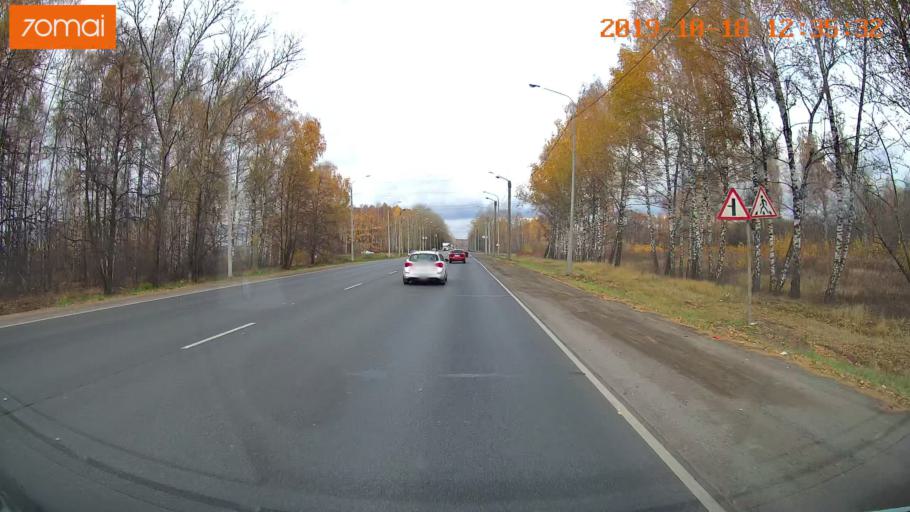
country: RU
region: Rjazan
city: Ryazan'
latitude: 54.6256
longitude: 39.6355
